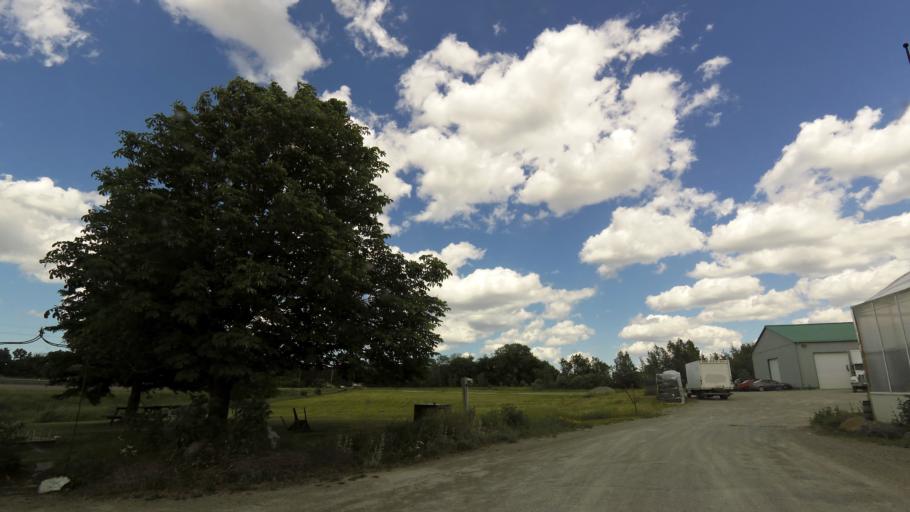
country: CA
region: Ontario
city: Uxbridge
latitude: 44.0436
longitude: -79.1834
